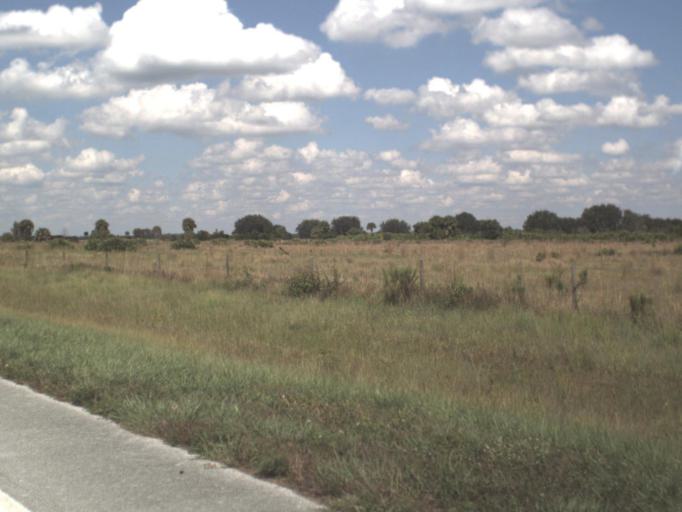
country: US
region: Florida
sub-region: Highlands County
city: Lake Placid
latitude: 27.4240
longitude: -81.2119
